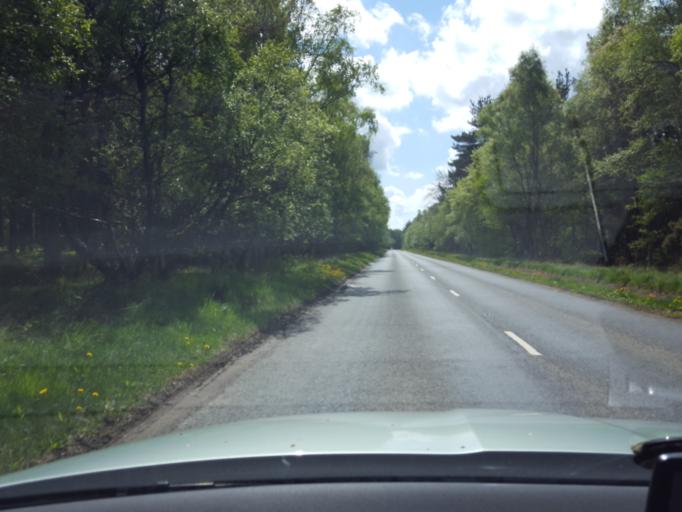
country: GB
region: Scotland
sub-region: Angus
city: Brechin
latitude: 56.7969
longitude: -2.6495
